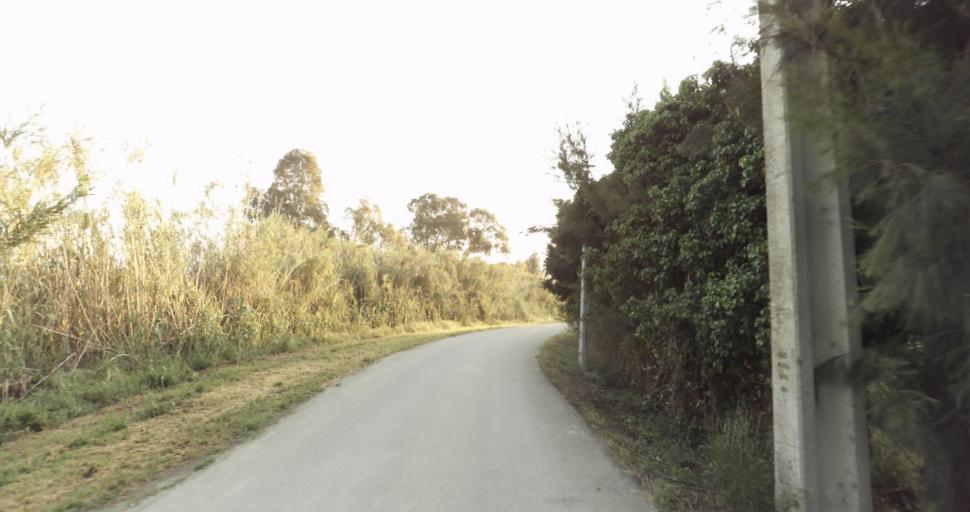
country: FR
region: Corsica
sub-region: Departement de la Haute-Corse
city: Biguglia
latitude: 42.6211
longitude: 9.4483
